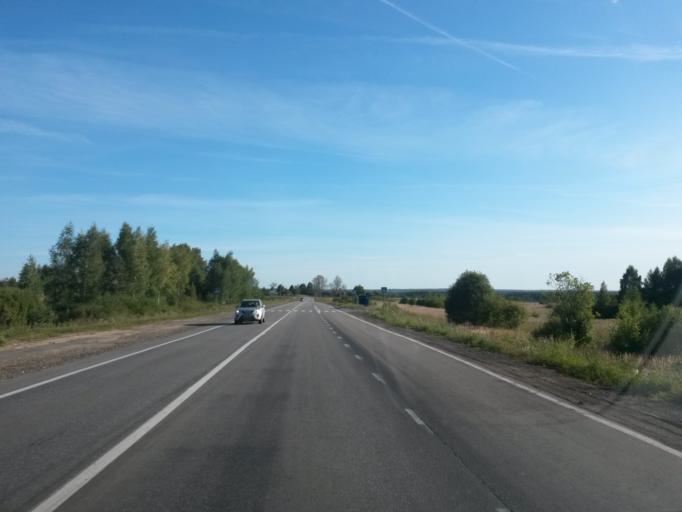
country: RU
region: Jaroslavl
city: Gavrilov-Yam
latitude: 57.3593
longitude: 39.9082
